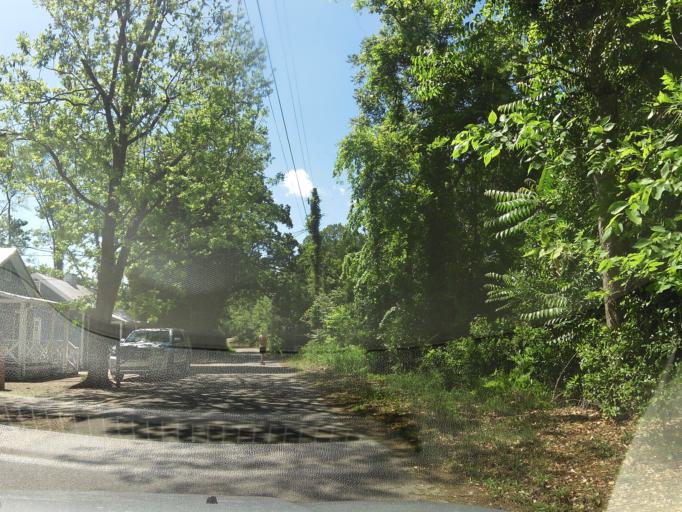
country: US
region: South Carolina
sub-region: Aiken County
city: Aiken
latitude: 33.5564
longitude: -81.7152
